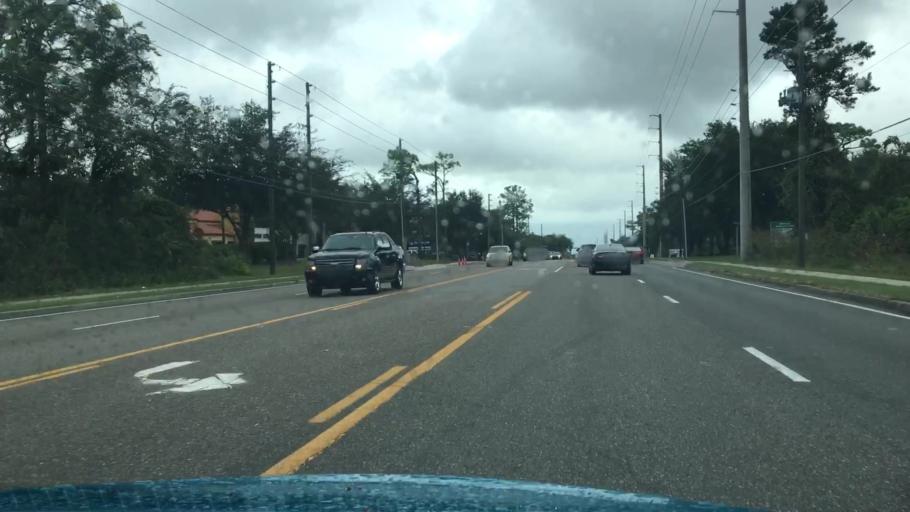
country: US
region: Florida
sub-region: Volusia County
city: Deltona
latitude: 28.9036
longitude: -81.2879
